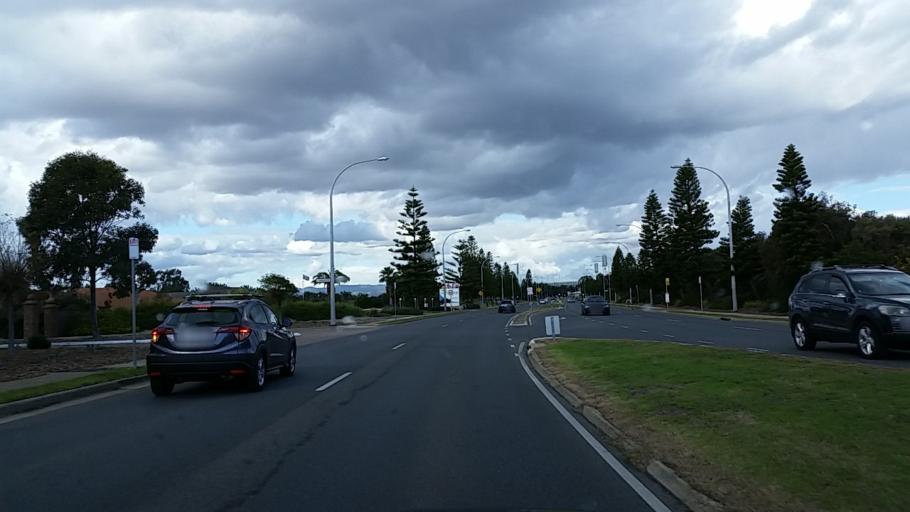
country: AU
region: South Australia
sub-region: Charles Sturt
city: West Lakes Shore
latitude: -34.8720
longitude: 138.4873
